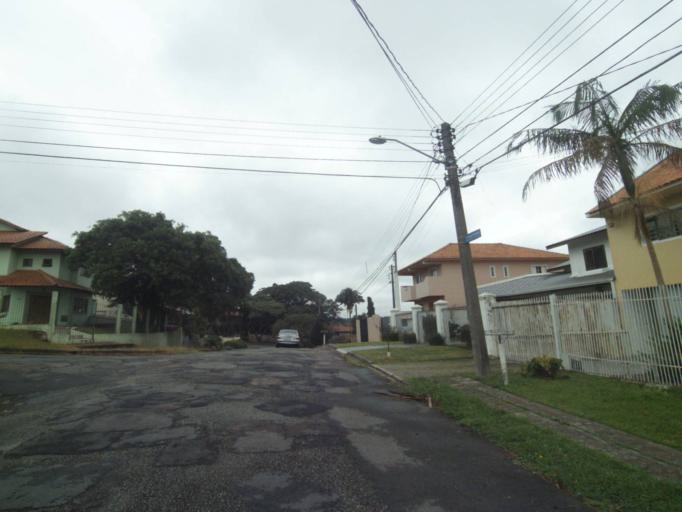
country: BR
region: Parana
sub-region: Curitiba
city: Curitiba
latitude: -25.4112
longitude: -49.2888
